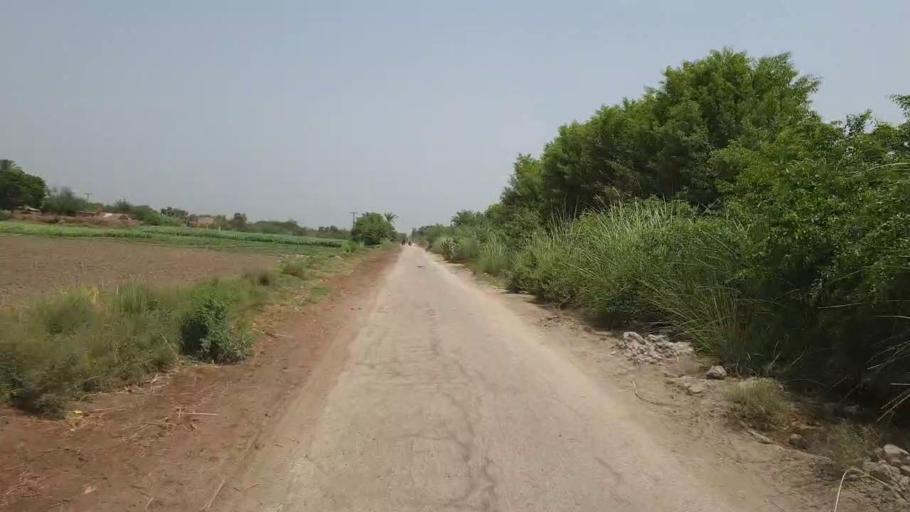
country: PK
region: Sindh
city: Nawabshah
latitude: 26.3004
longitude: 68.3051
